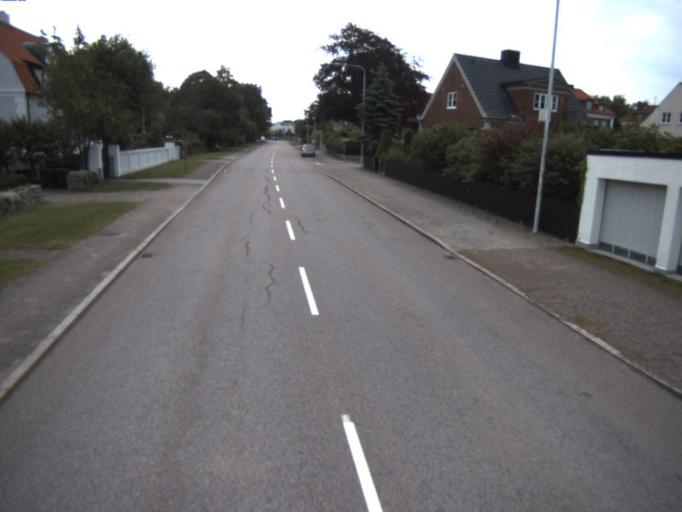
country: SE
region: Skane
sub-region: Helsingborg
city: Helsingborg
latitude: 56.0632
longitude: 12.6891
